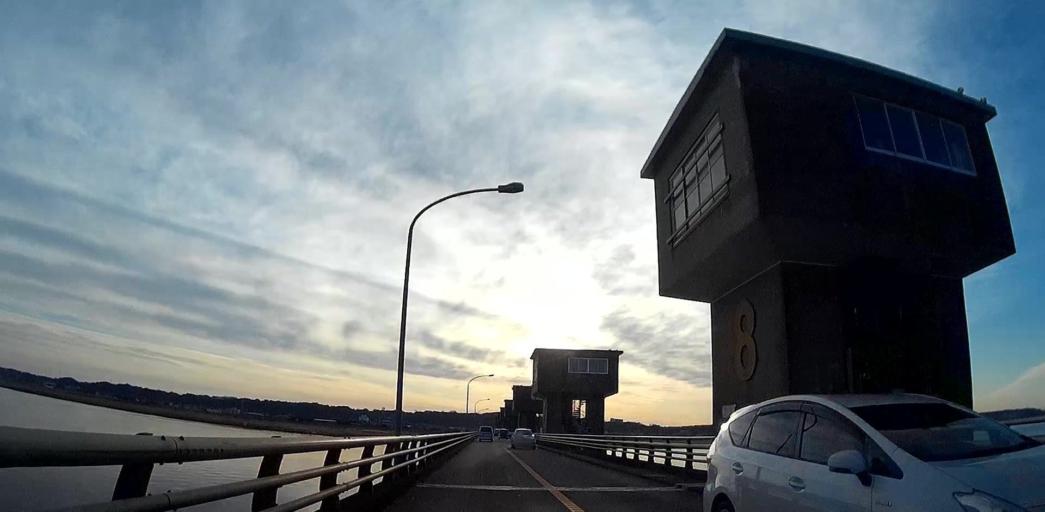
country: JP
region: Chiba
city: Omigawa
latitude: 35.8382
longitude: 140.7045
